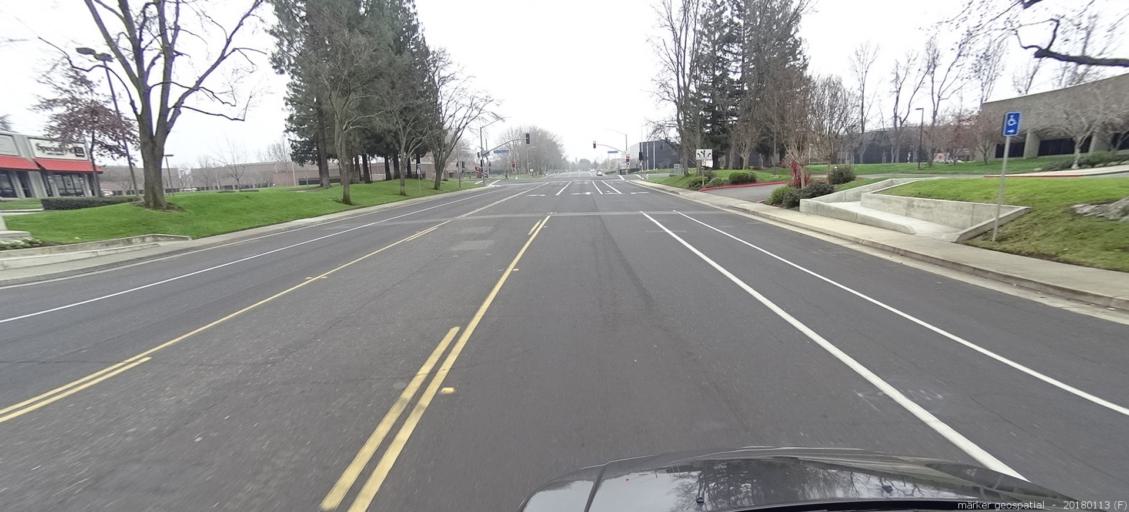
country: US
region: California
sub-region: Sacramento County
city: Rancho Cordova
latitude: 38.5905
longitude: -121.2761
